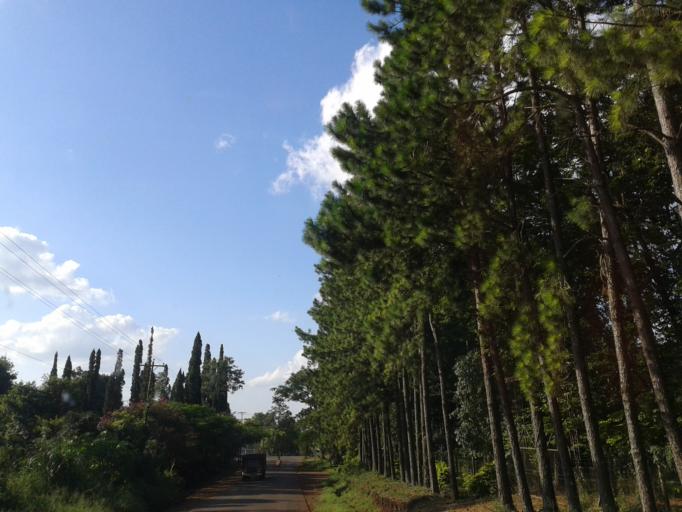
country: AR
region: Misiones
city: Guarani
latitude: -27.4946
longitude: -55.1597
